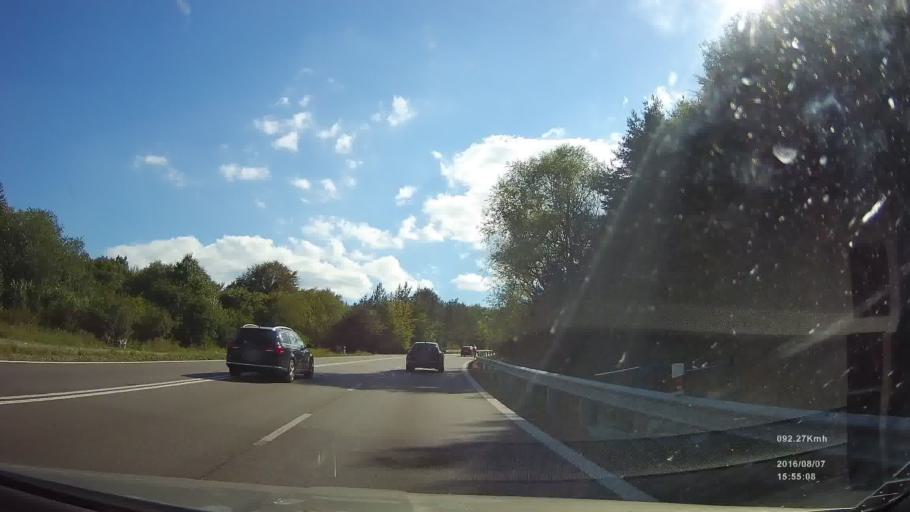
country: SK
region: Presovsky
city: Giraltovce
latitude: 49.0780
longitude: 21.4415
